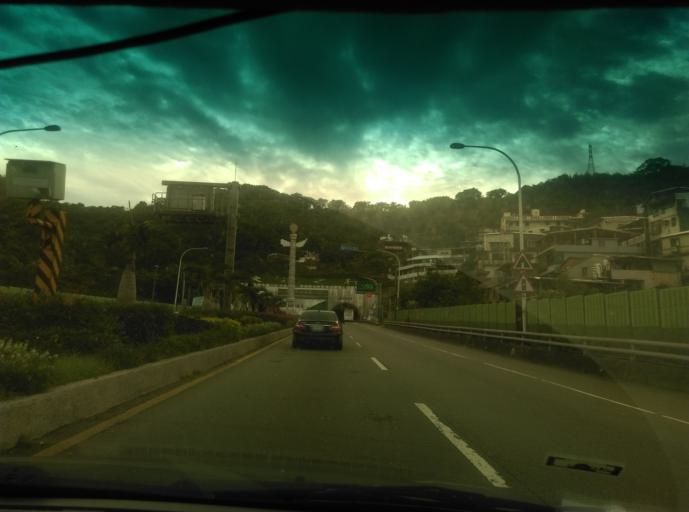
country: TW
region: Taiwan
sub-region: Keelung
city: Keelung
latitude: 25.1239
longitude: 121.7363
